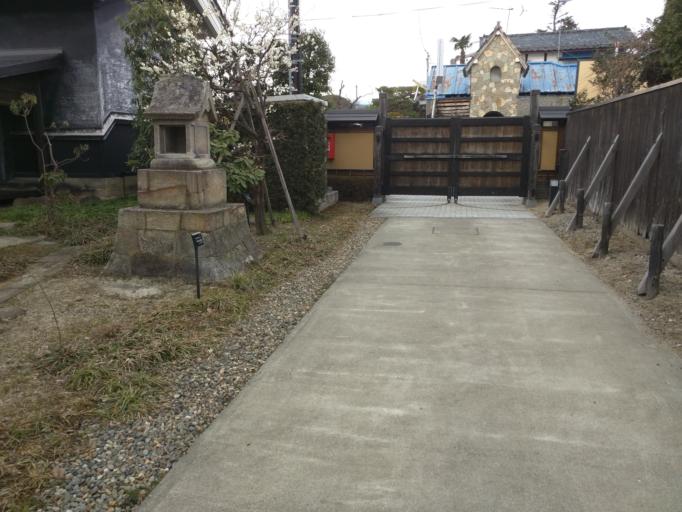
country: JP
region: Fukushima
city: Fukushima-shi
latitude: 37.8335
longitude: 140.4524
